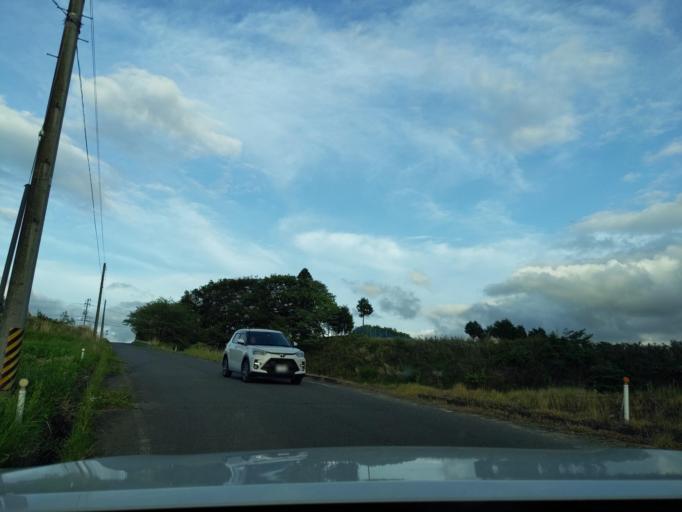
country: JP
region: Fukushima
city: Miharu
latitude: 37.4120
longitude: 140.4694
